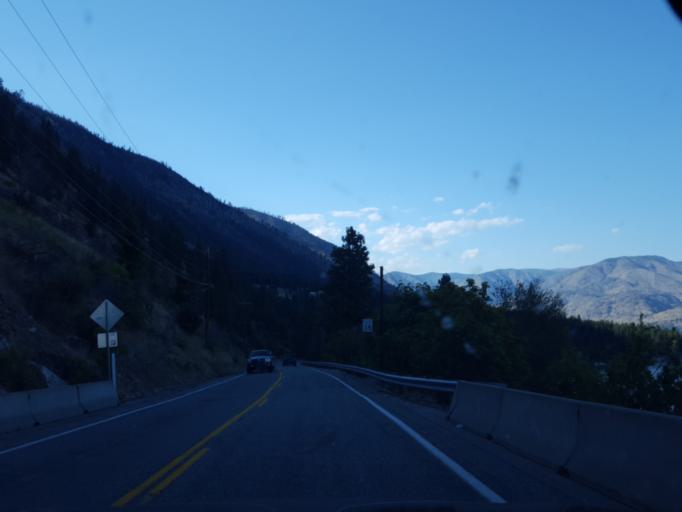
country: US
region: Washington
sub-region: Chelan County
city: Granite Falls
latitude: 47.9025
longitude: -120.2152
